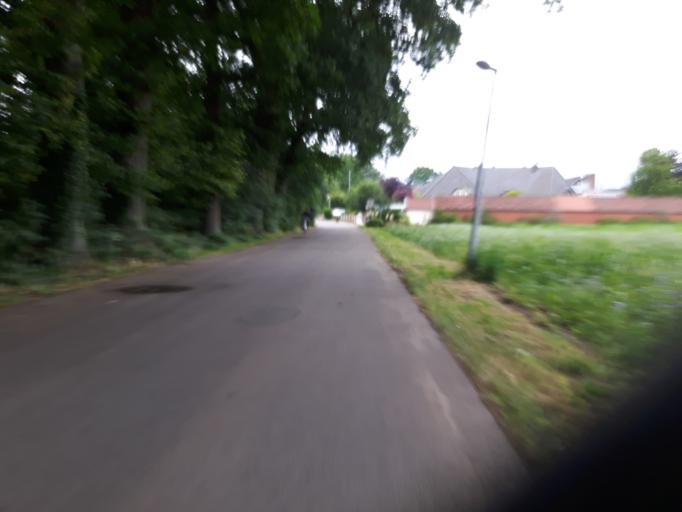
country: DE
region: Lower Saxony
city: Stuhr
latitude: 53.0316
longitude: 8.7037
